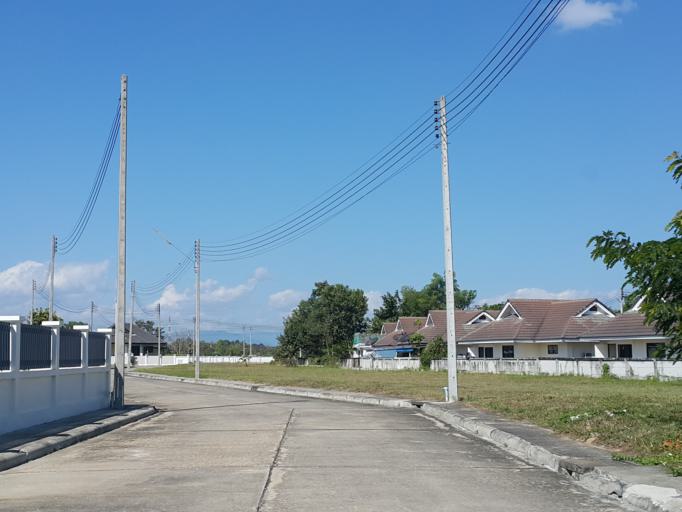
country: TH
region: Chiang Mai
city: San Sai
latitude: 18.9451
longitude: 98.9237
